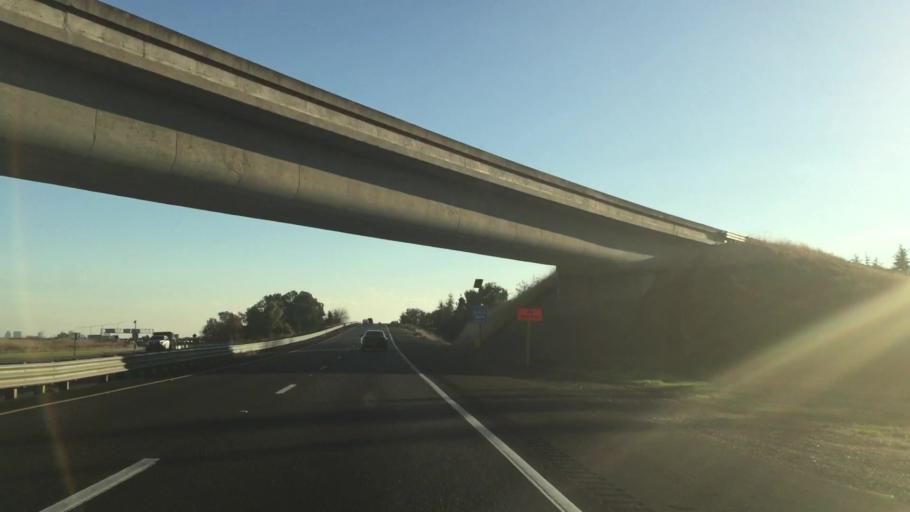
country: US
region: California
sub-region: Sacramento County
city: Elverta
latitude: 38.6709
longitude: -121.5403
